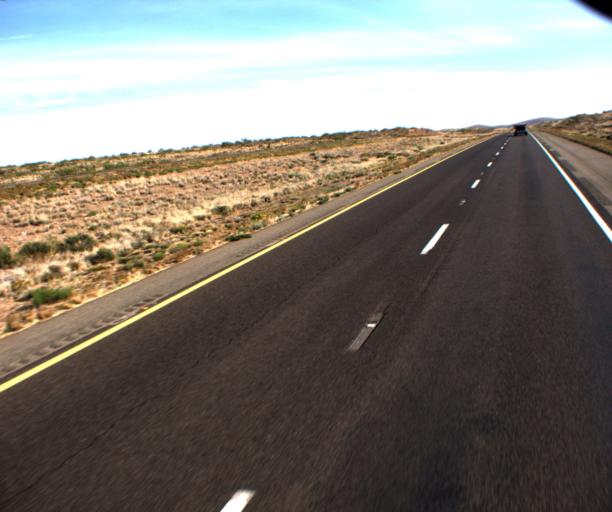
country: US
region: Arizona
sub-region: Cochise County
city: Willcox
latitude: 32.3671
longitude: -109.6778
